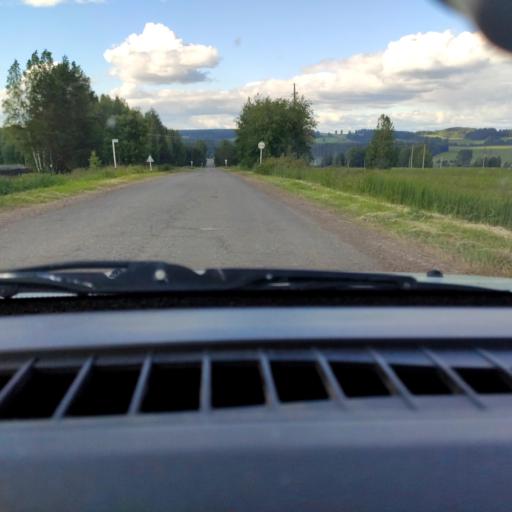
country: RU
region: Perm
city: Kukushtan
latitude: 57.2942
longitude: 56.5368
